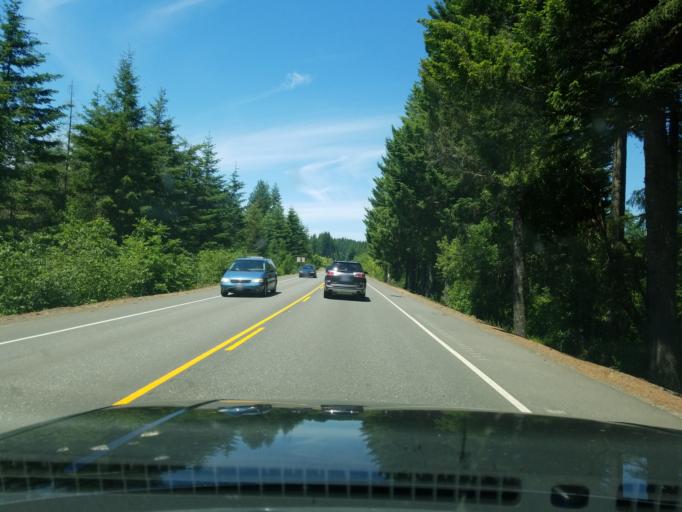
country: US
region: Oregon
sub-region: Columbia County
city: Vernonia
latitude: 45.7364
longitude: -123.2596
